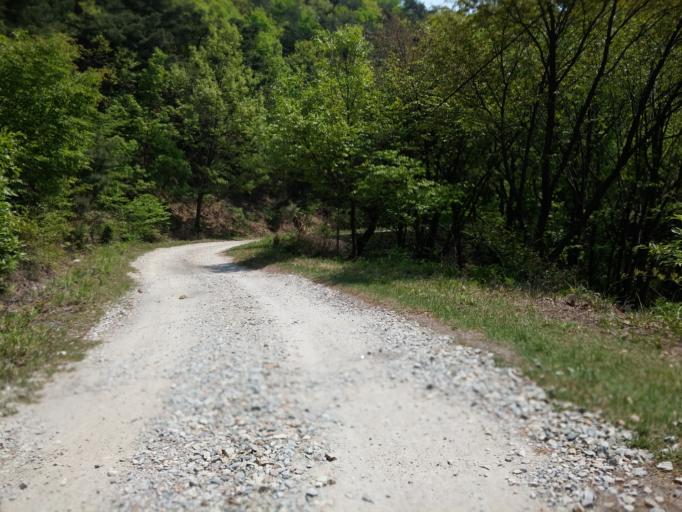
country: KR
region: Chungcheongbuk-do
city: Okcheon
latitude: 36.4194
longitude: 127.5942
